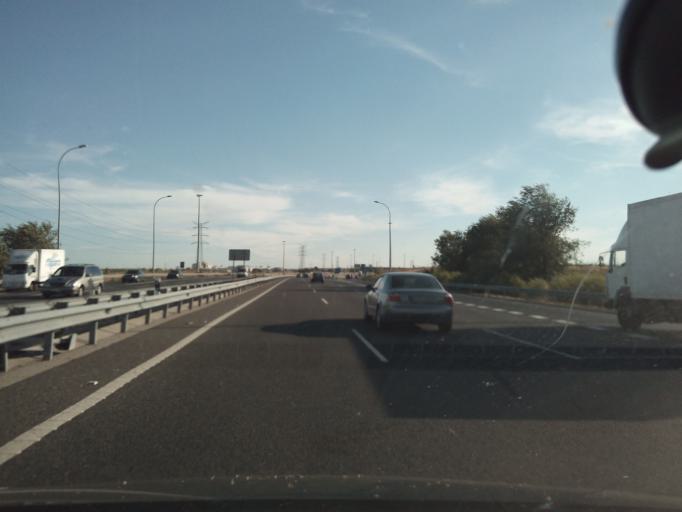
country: ES
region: Madrid
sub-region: Provincia de Madrid
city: Pinto
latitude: 40.2850
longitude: -3.6809
